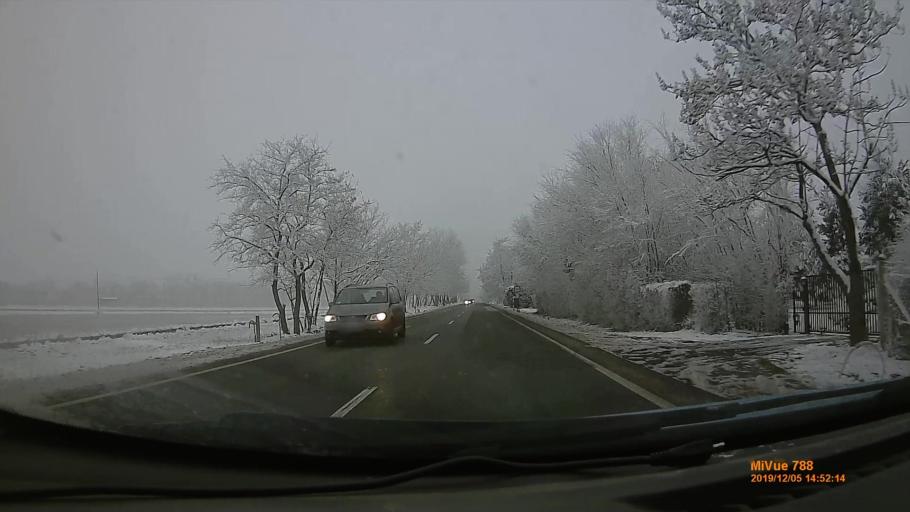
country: HU
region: Szabolcs-Szatmar-Bereg
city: Nyirtelek
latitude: 47.9995
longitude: 21.6471
